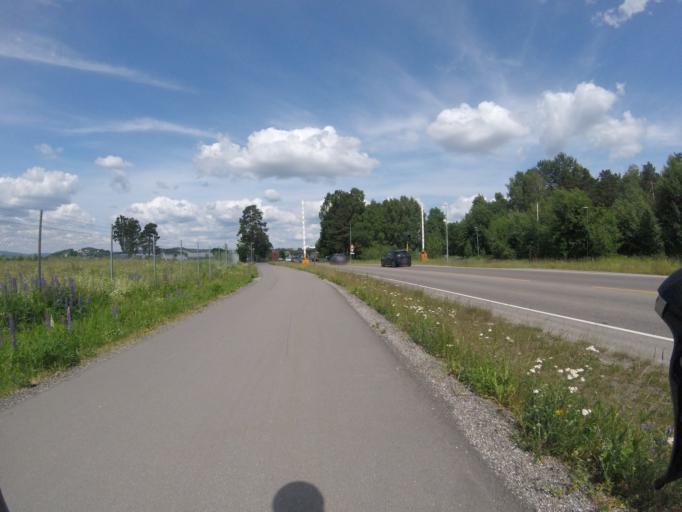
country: NO
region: Akershus
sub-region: Skedsmo
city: Lillestrom
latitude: 59.9661
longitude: 11.0521
